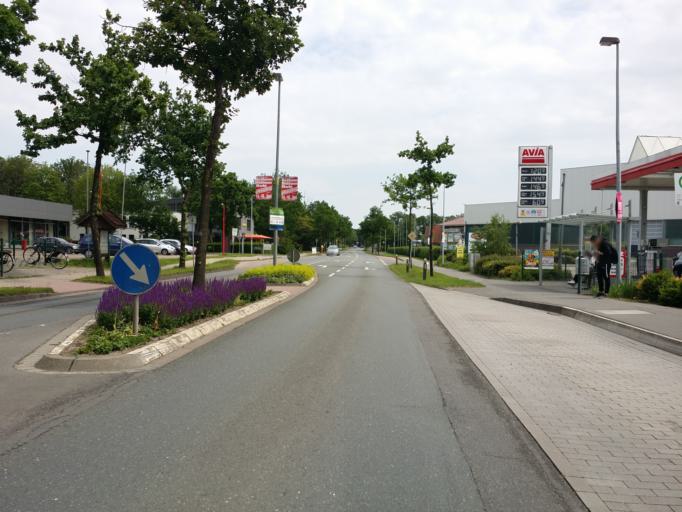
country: DE
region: Lower Saxony
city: Wiefelstede
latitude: 53.2508
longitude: 8.1200
